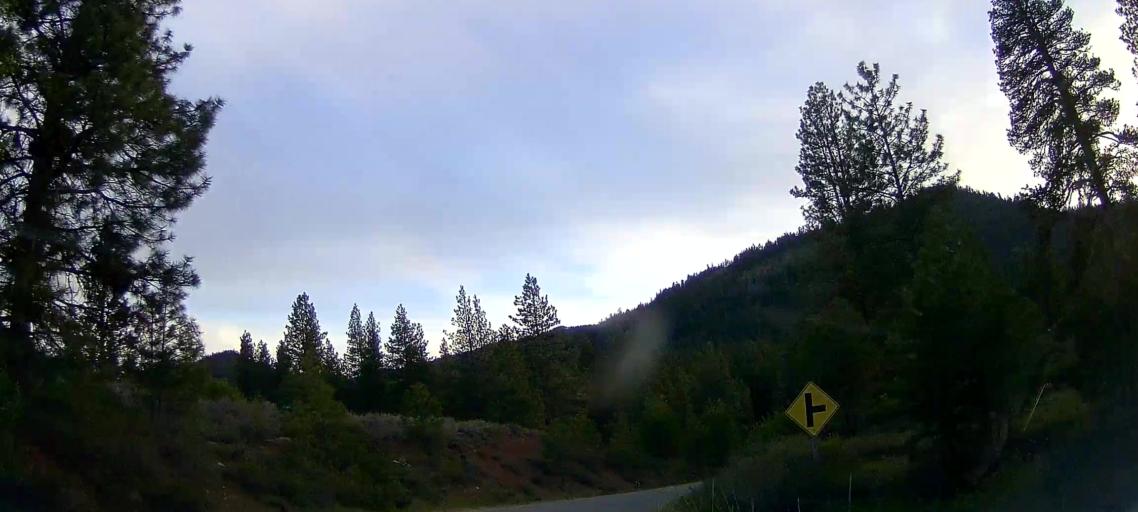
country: US
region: Washington
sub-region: Chelan County
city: Granite Falls
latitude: 48.4660
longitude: -120.2595
